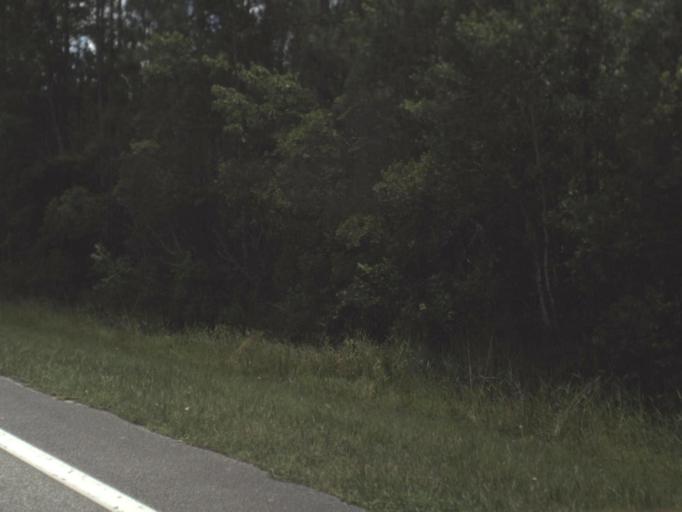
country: US
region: Florida
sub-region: Levy County
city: Bronson
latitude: 29.3787
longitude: -82.7130
